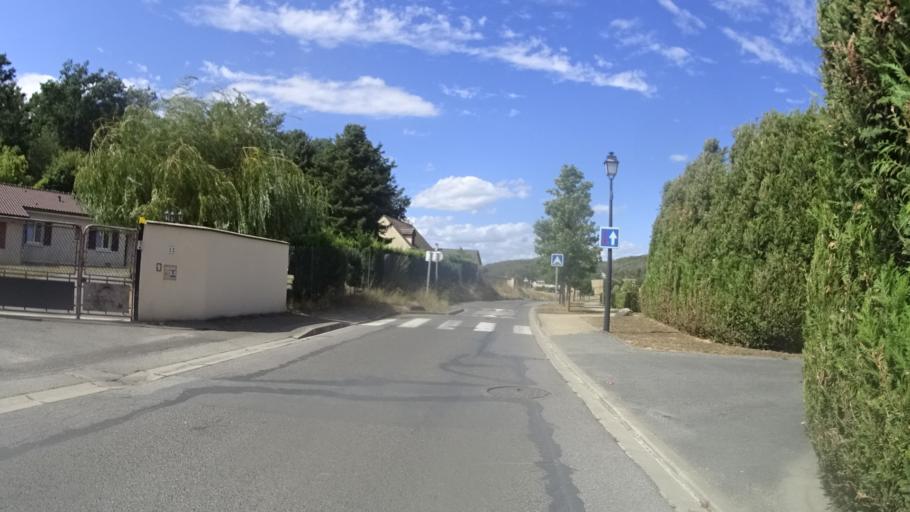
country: FR
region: Ile-de-France
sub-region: Departement de l'Essonne
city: Boutigny-sur-Essonne
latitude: 48.4219
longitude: 2.3894
